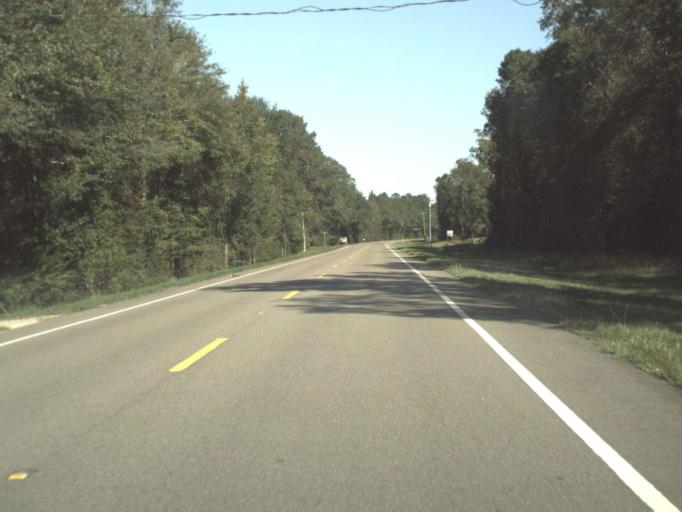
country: US
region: Florida
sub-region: Walton County
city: DeFuniak Springs
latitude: 30.6929
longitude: -85.9364
